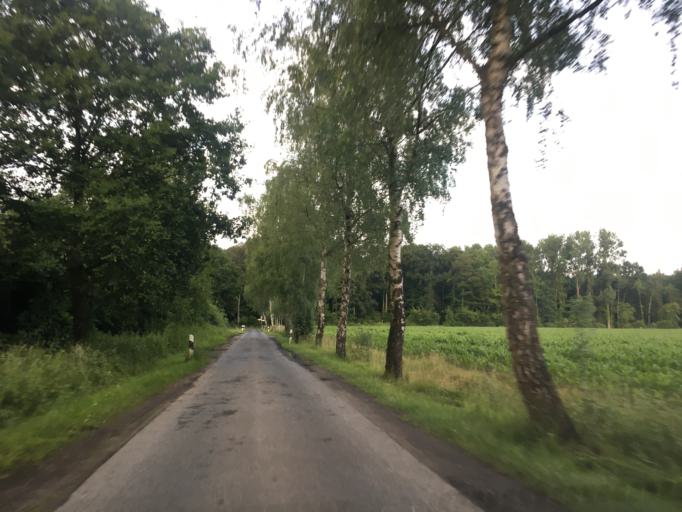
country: DE
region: North Rhine-Westphalia
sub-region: Regierungsbezirk Munster
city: Muenster
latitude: 51.9099
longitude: 7.5678
